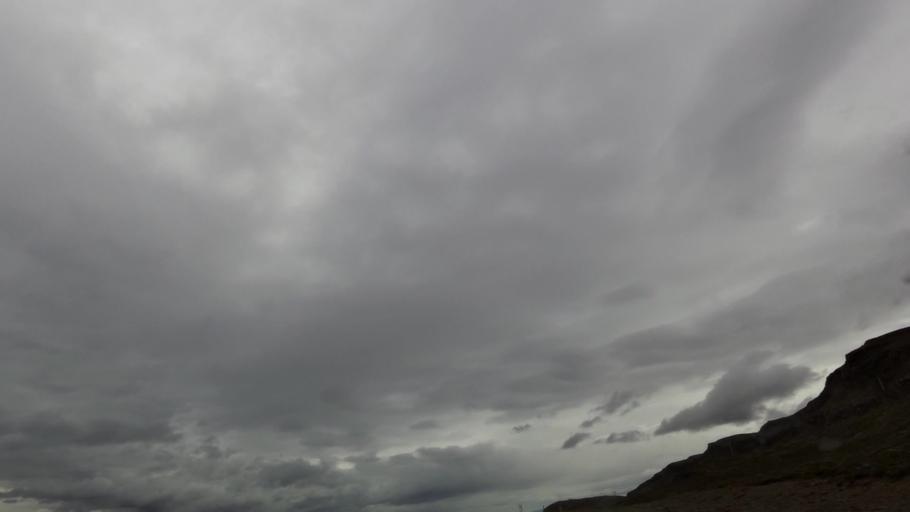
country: IS
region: West
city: Stykkisholmur
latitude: 65.0386
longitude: -22.4795
